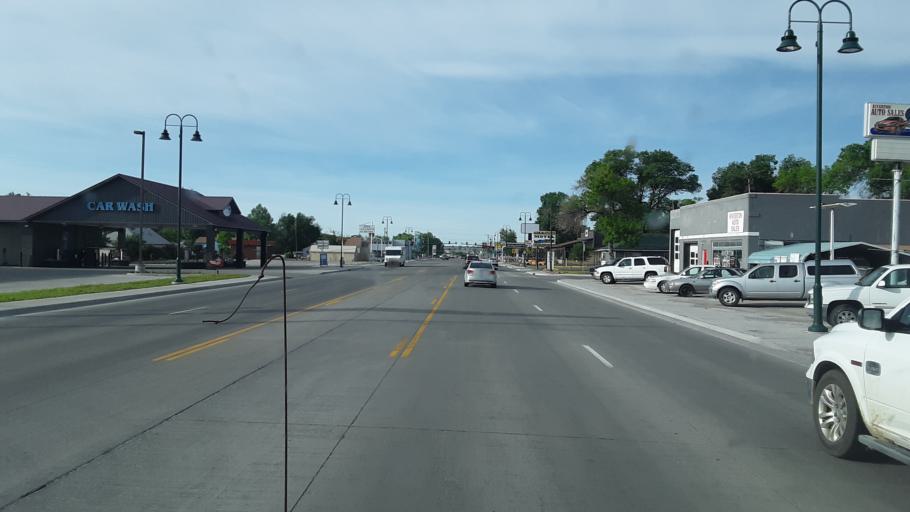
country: US
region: Wyoming
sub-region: Fremont County
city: Riverton
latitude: 43.0294
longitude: -108.3807
